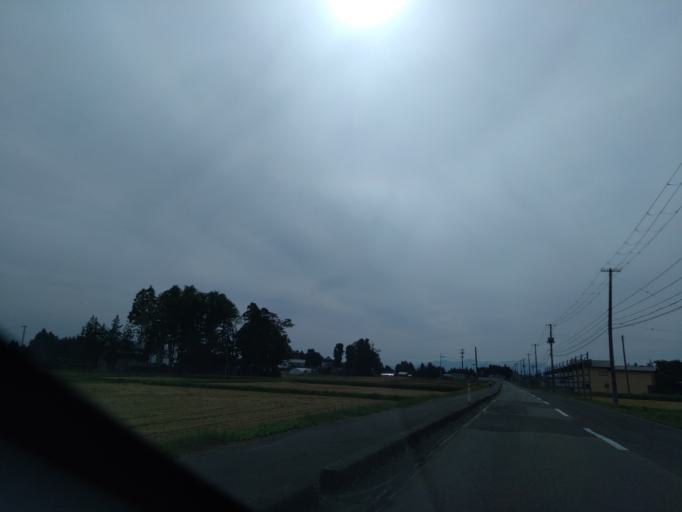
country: JP
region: Iwate
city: Hanamaki
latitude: 39.4434
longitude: 141.0847
